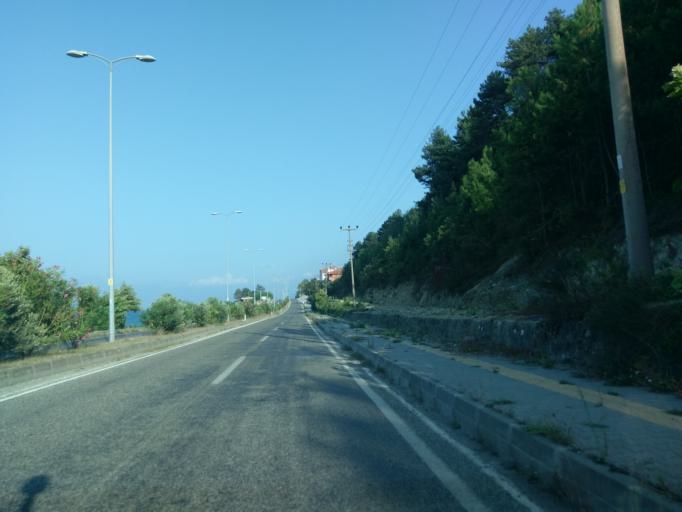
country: TR
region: Kastamonu
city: Catalzeytin
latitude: 41.9558
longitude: 34.1979
